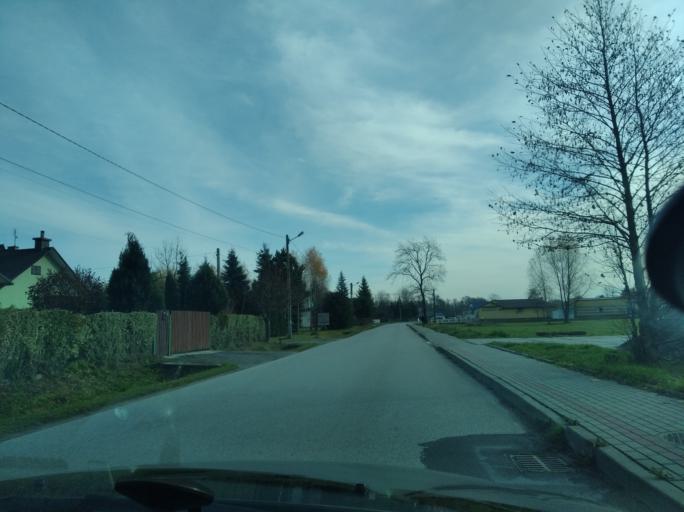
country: PL
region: Subcarpathian Voivodeship
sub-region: Powiat lancucki
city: Kraczkowa
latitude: 50.0397
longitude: 22.1885
